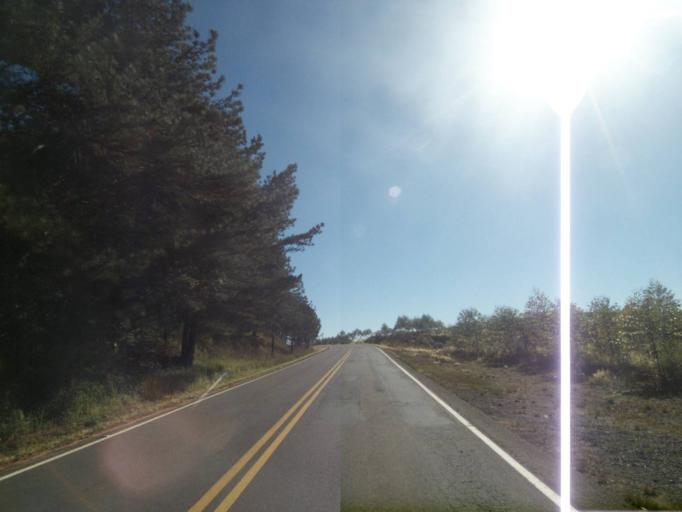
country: BR
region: Parana
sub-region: Telemaco Borba
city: Telemaco Borba
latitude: -24.4223
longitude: -50.5837
